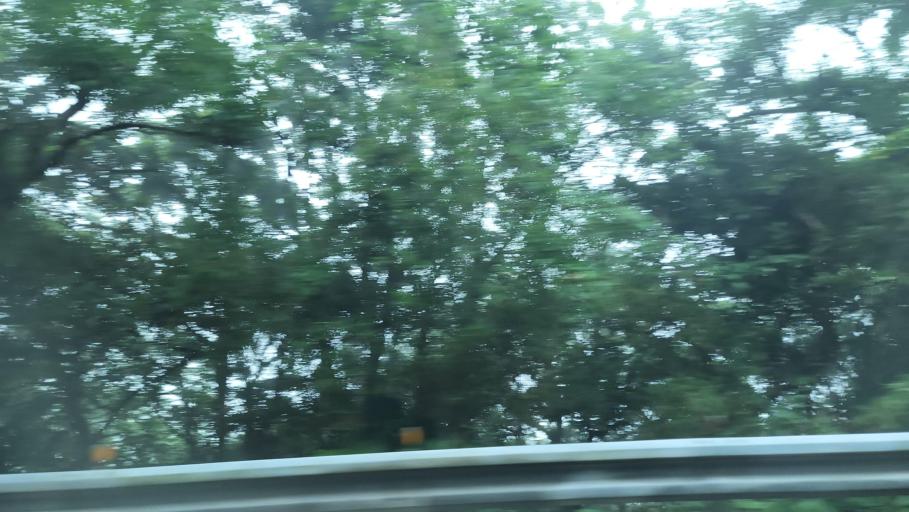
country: TW
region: Taipei
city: Taipei
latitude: 25.1422
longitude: 121.6029
